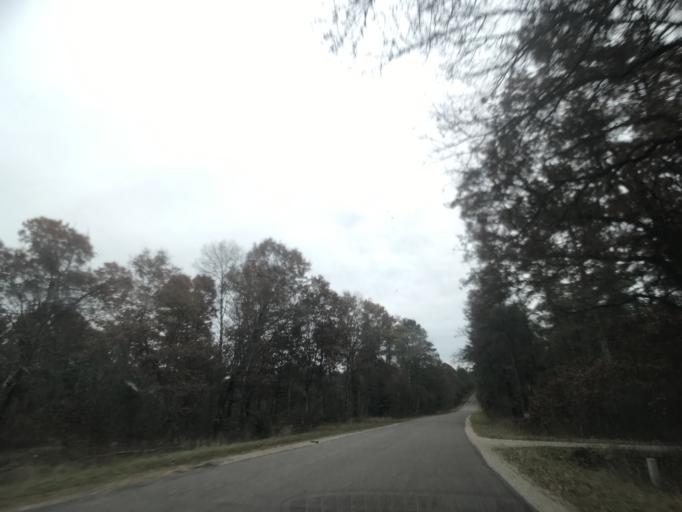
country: US
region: Wisconsin
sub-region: Oconto County
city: Gillett
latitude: 45.2627
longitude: -88.2526
